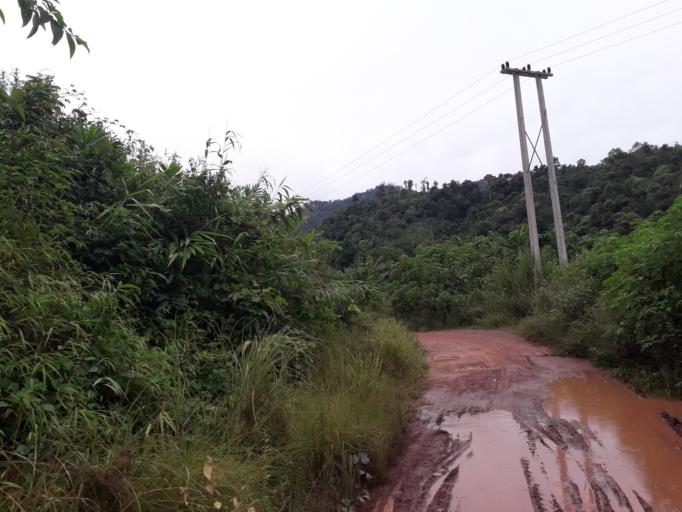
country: CN
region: Yunnan
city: Menglie
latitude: 22.2447
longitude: 101.6093
